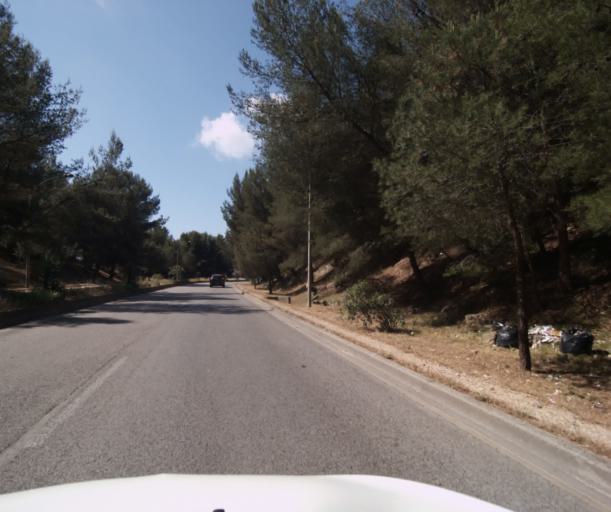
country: FR
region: Provence-Alpes-Cote d'Azur
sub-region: Departement du Var
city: La Seyne-sur-Mer
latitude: 43.1225
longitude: 5.8905
